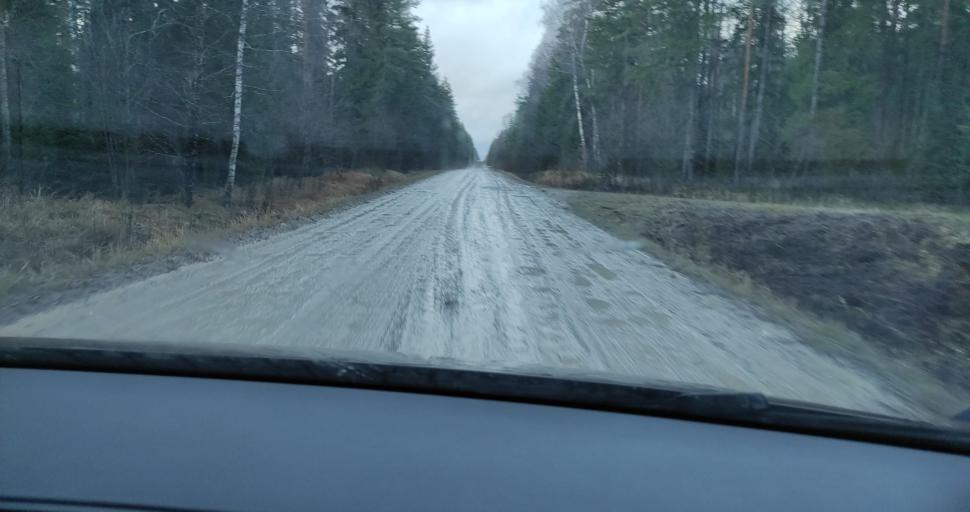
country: LV
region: Skrunda
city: Skrunda
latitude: 56.7283
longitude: 22.2033
